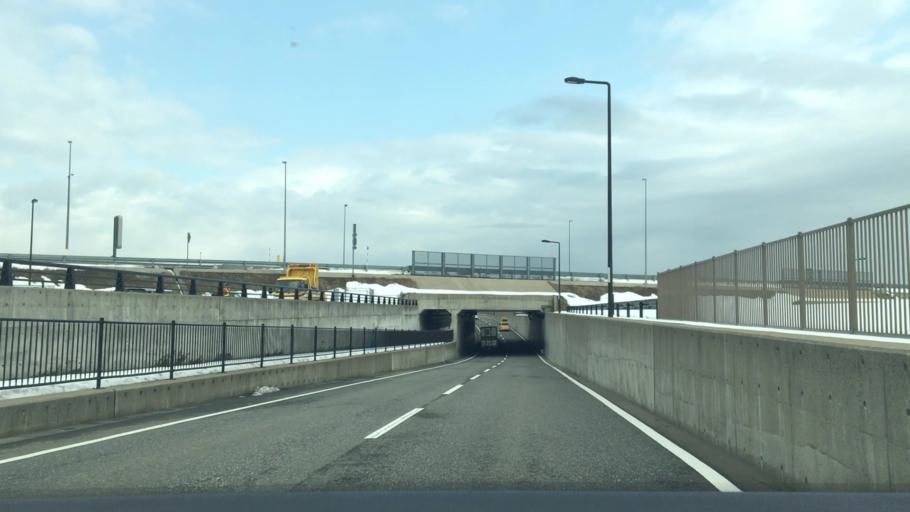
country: JP
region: Ishikawa
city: Matsuto
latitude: 36.5522
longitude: 136.5799
